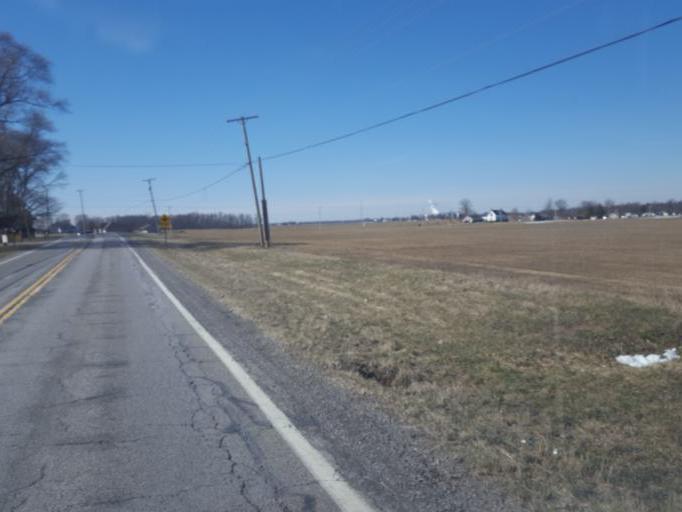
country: US
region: Ohio
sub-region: Marion County
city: Marion
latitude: 40.6468
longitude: -83.1223
